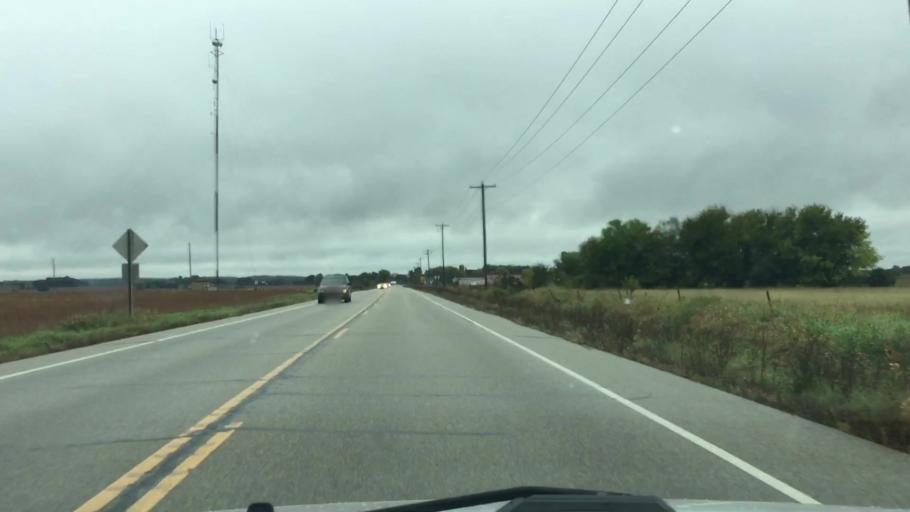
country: US
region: Wisconsin
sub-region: Walworth County
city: Whitewater
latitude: 42.8139
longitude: -88.7565
